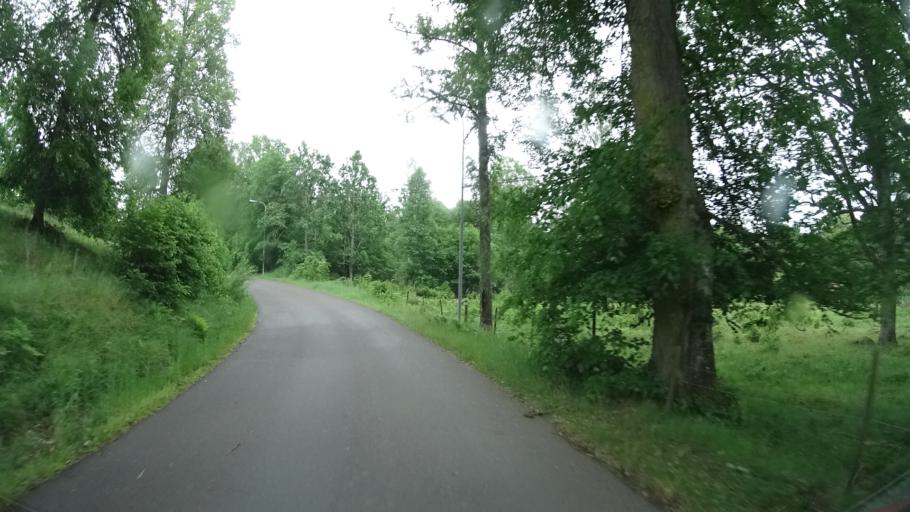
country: SE
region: Joenkoeping
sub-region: Eksjo Kommun
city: Mariannelund
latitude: 57.6787
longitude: 15.5814
